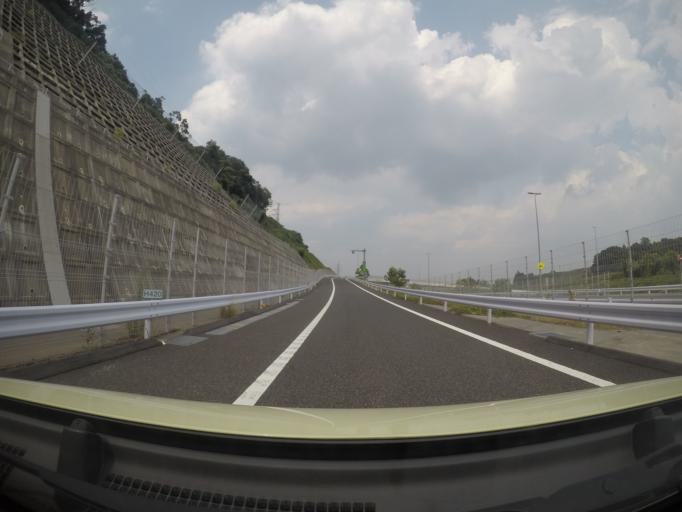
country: JP
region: Tokyo
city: Hachioji
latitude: 35.5794
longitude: 139.2877
